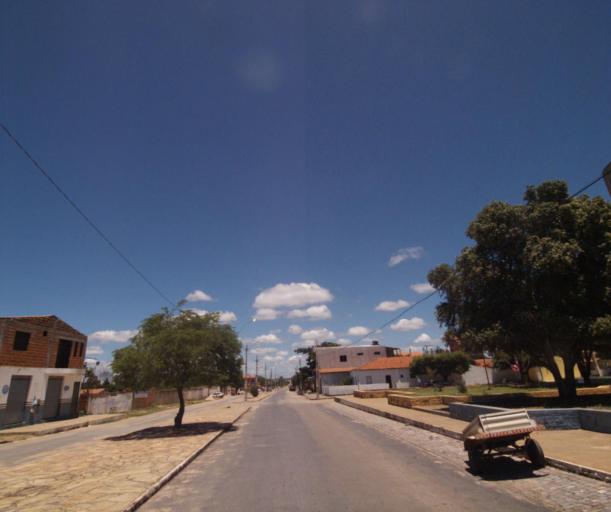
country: BR
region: Bahia
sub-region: Carinhanha
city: Carinhanha
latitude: -14.2976
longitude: -43.7724
